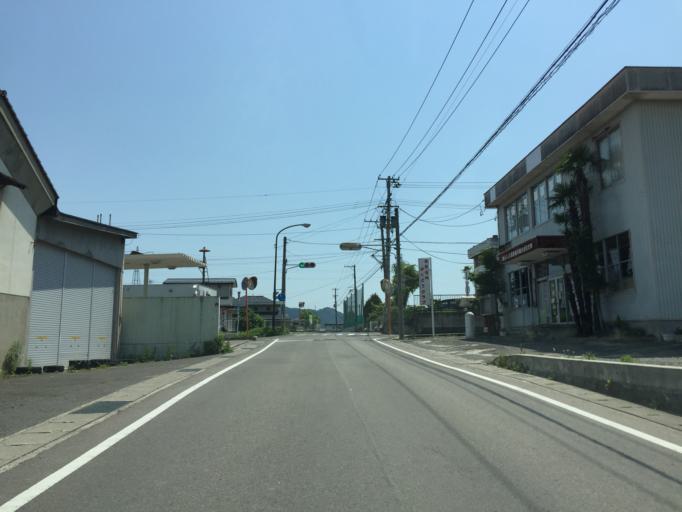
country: JP
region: Fukushima
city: Fukushima-shi
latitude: 37.8072
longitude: 140.4740
